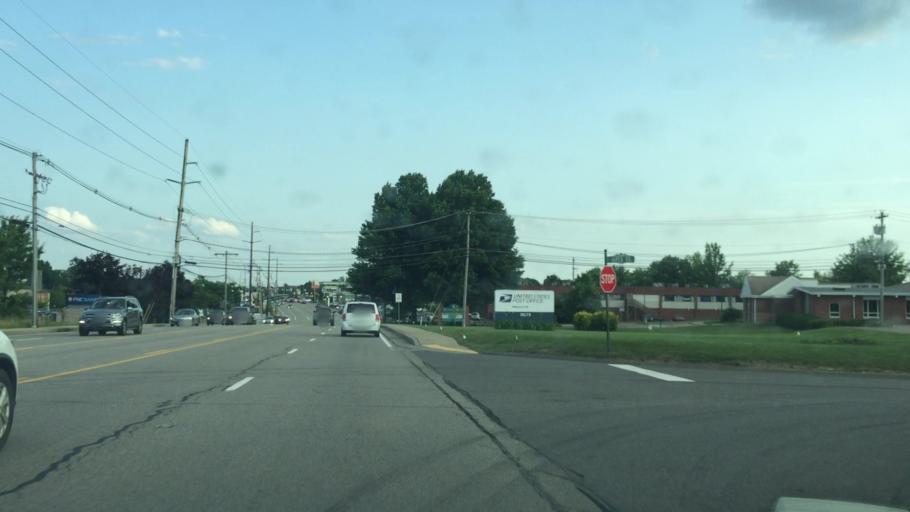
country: US
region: Pennsylvania
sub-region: Allegheny County
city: Bradford Woods
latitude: 40.6143
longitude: -80.0550
